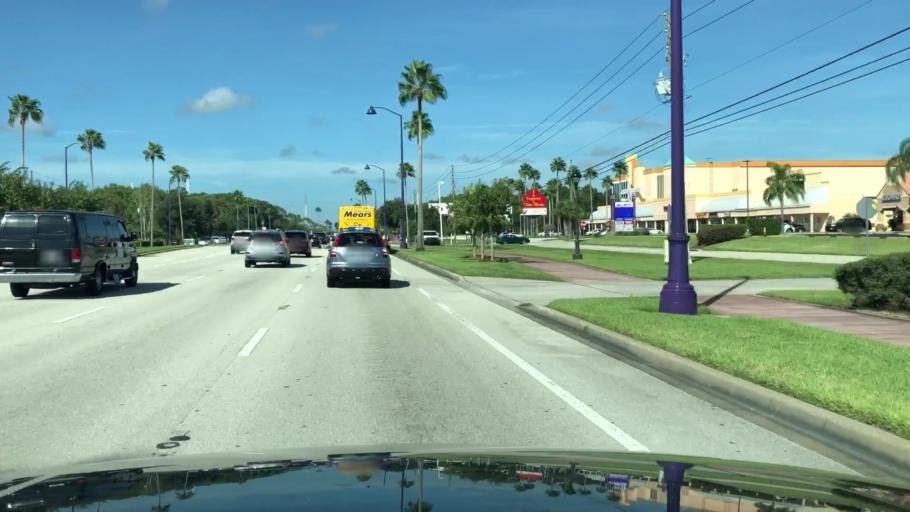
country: US
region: Florida
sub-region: Osceola County
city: Celebration
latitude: 28.3330
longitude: -81.5009
